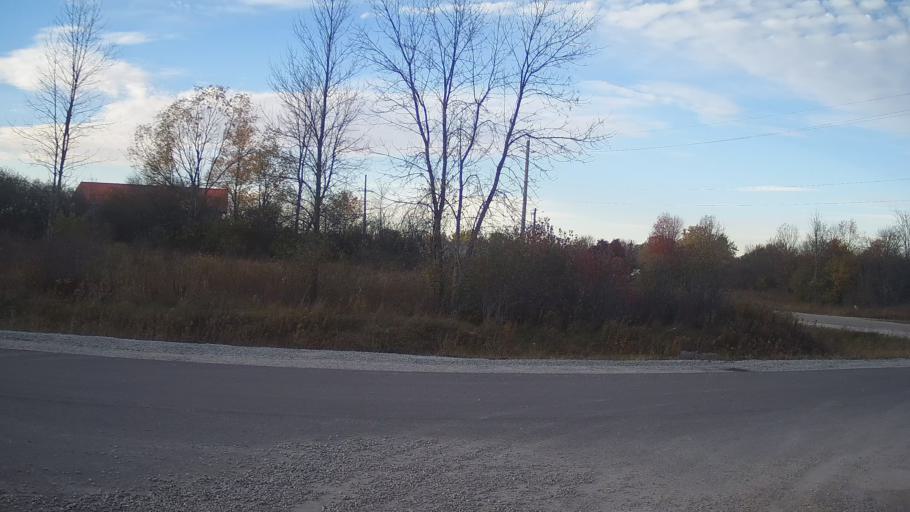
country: CA
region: Ontario
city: Perth
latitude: 44.8842
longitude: -76.2403
